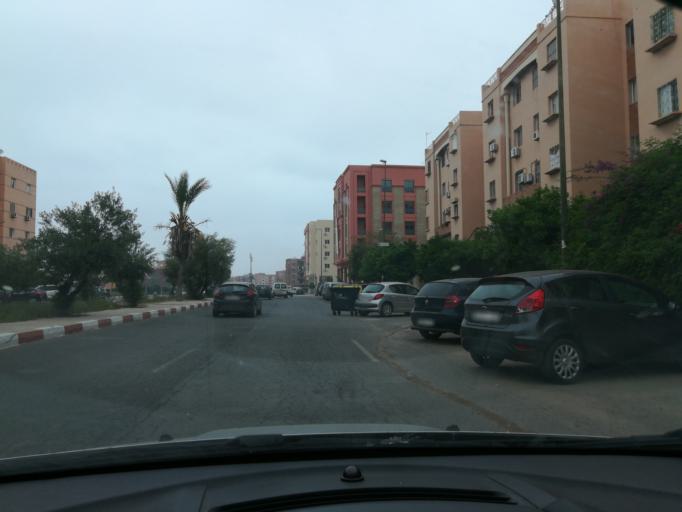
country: MA
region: Marrakech-Tensift-Al Haouz
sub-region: Marrakech
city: Marrakesh
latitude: 31.6664
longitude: -8.0306
